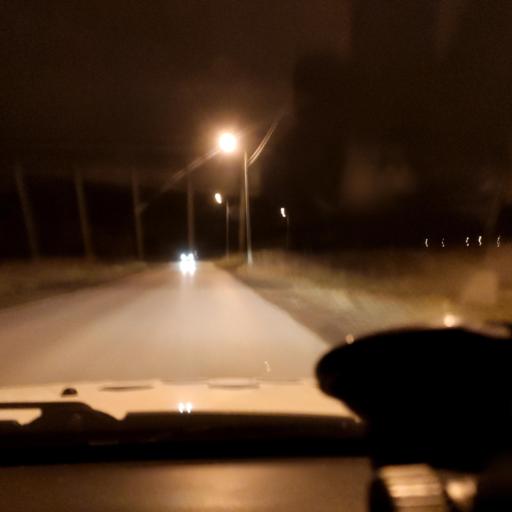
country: RU
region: Perm
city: Perm
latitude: 58.0195
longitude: 56.3369
